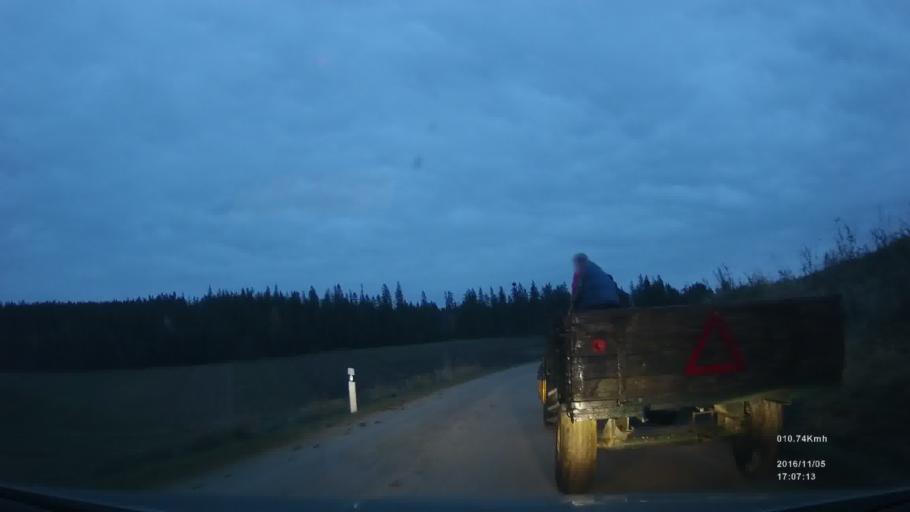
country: SK
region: Presovsky
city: Lubica
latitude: 49.0484
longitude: 20.5057
